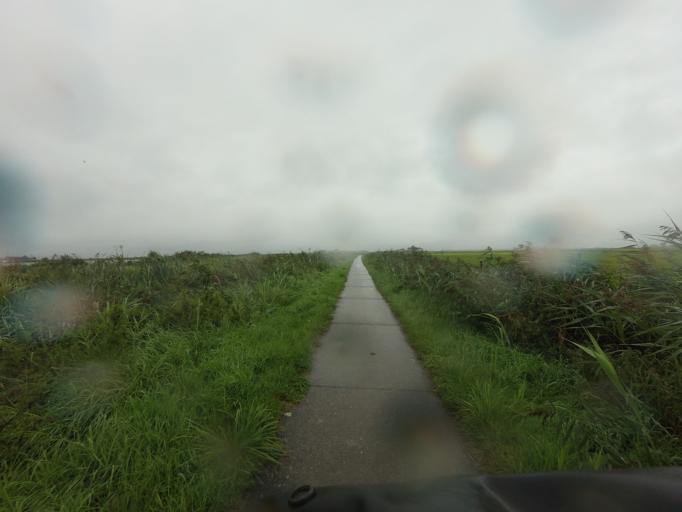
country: NL
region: Friesland
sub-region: Sudwest Fryslan
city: Workum
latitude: 52.9981
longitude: 5.5055
